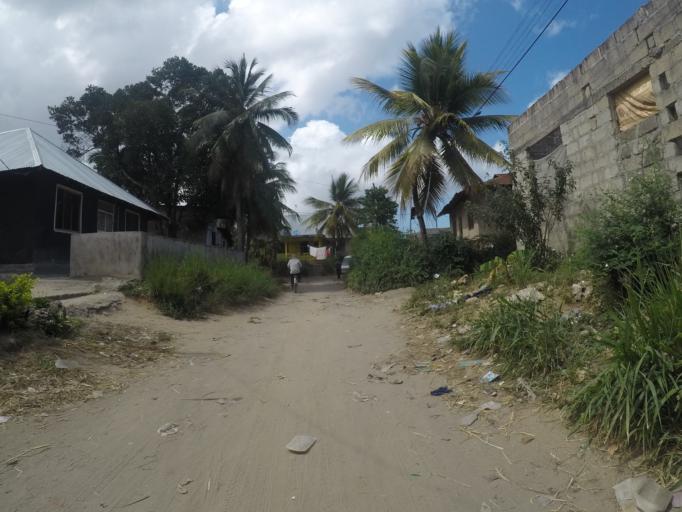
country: TZ
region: Zanzibar Urban/West
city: Zanzibar
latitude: -6.1776
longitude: 39.2120
